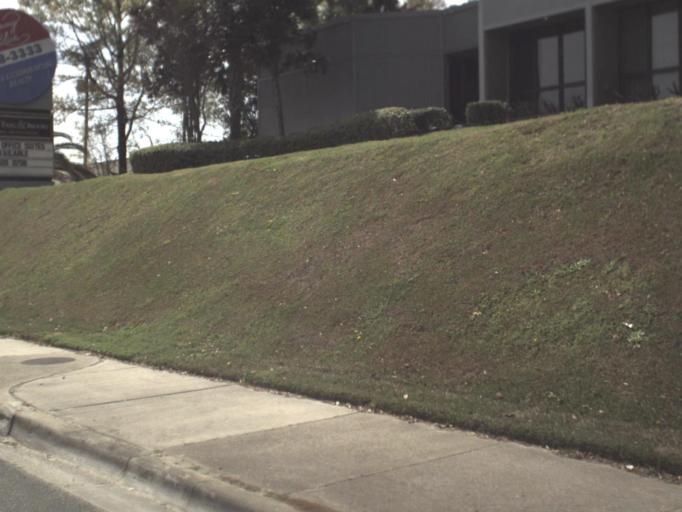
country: US
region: Florida
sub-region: Leon County
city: Tallahassee
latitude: 30.4982
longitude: -84.2470
